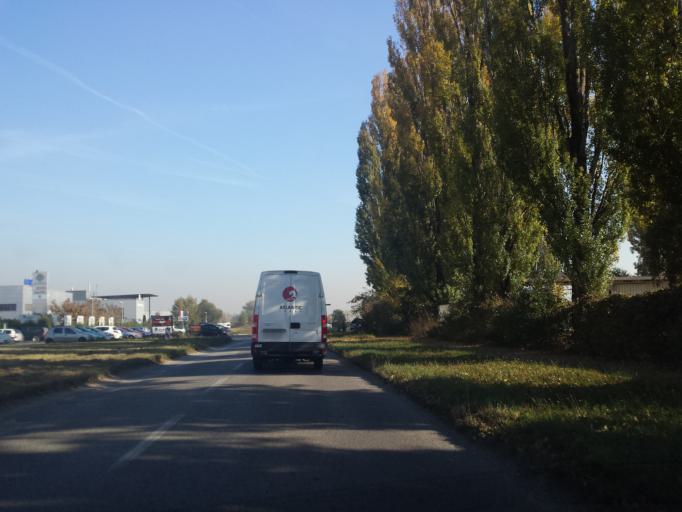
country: HR
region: Grad Zagreb
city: Stenjevec
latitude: 45.8059
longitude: 15.8630
